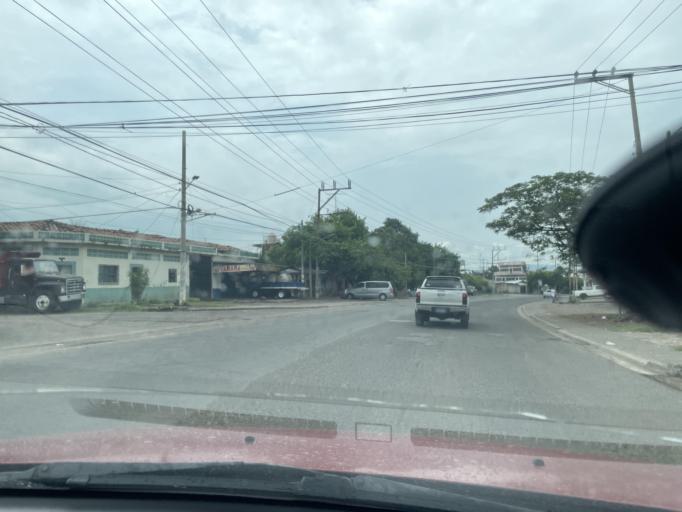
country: SV
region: La Union
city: Santa Rosa de Lima
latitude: 13.6315
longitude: -87.8897
